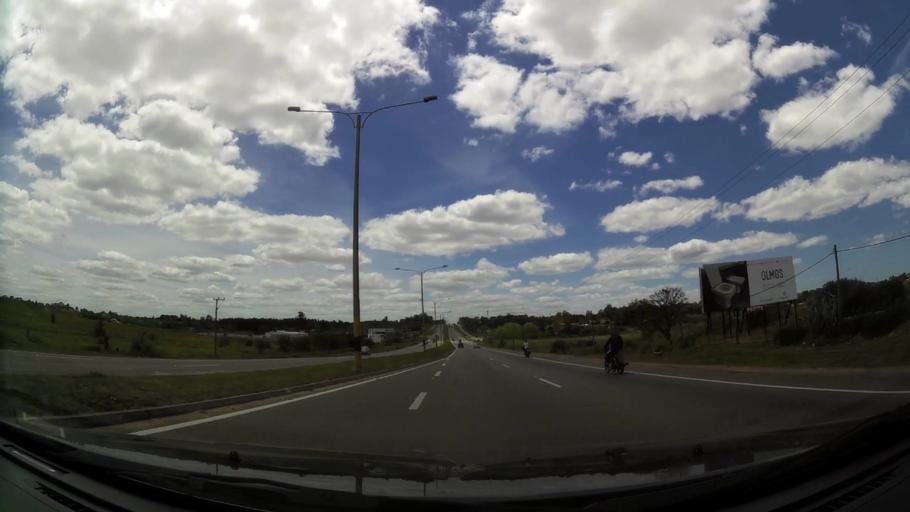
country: UY
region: Canelones
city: Colonia Nicolich
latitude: -34.8261
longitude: -55.9997
